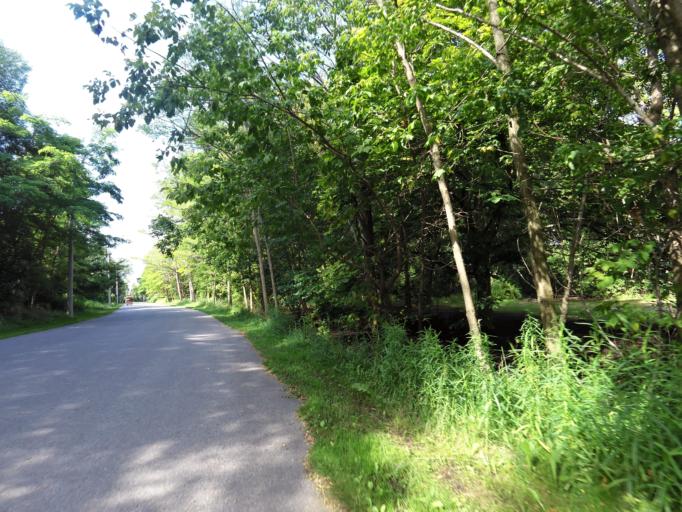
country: CA
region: Ontario
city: Toronto
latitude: 43.6203
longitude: -79.3666
